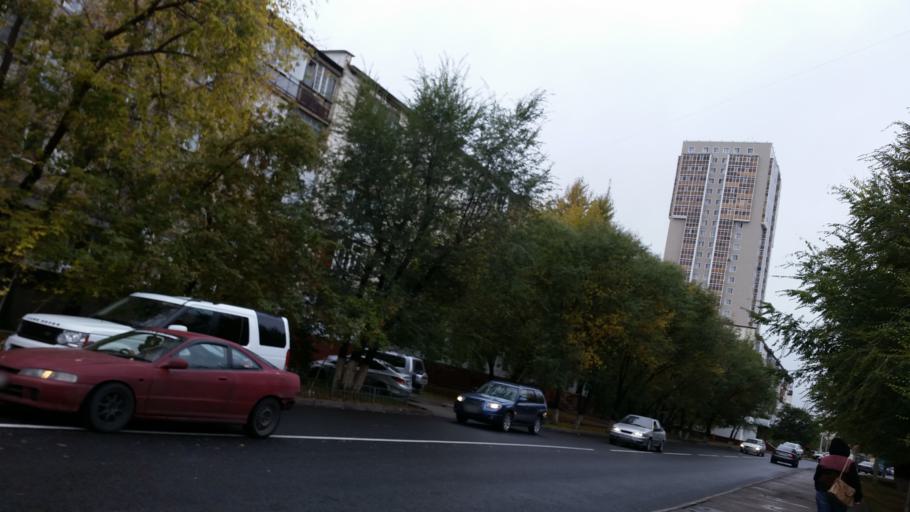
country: KZ
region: Astana Qalasy
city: Astana
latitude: 51.1491
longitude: 71.4656
